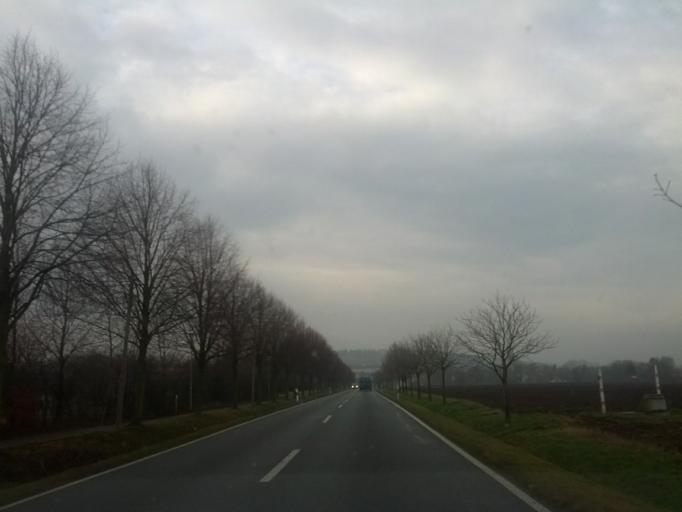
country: DE
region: Thuringia
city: Warza
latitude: 50.9938
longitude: 10.6712
